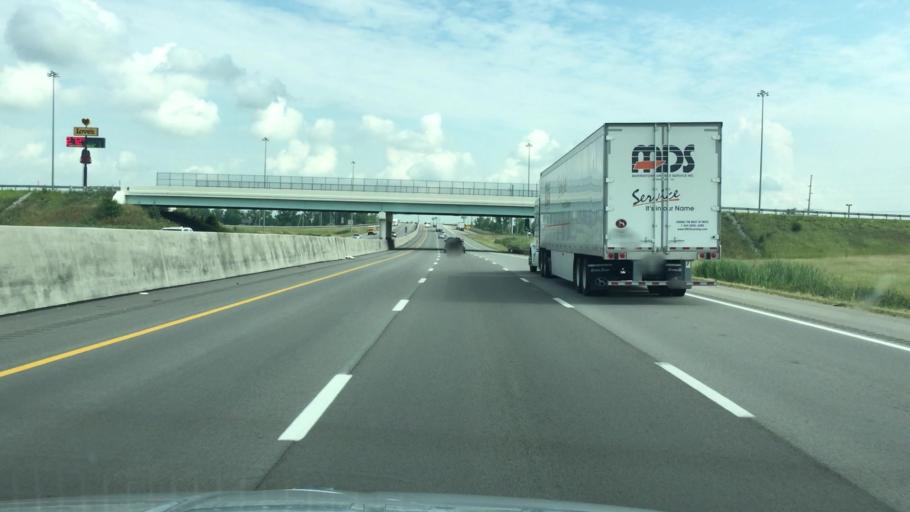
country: US
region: Ohio
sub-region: Wood County
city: North Baltimore
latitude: 41.1714
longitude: -83.6492
